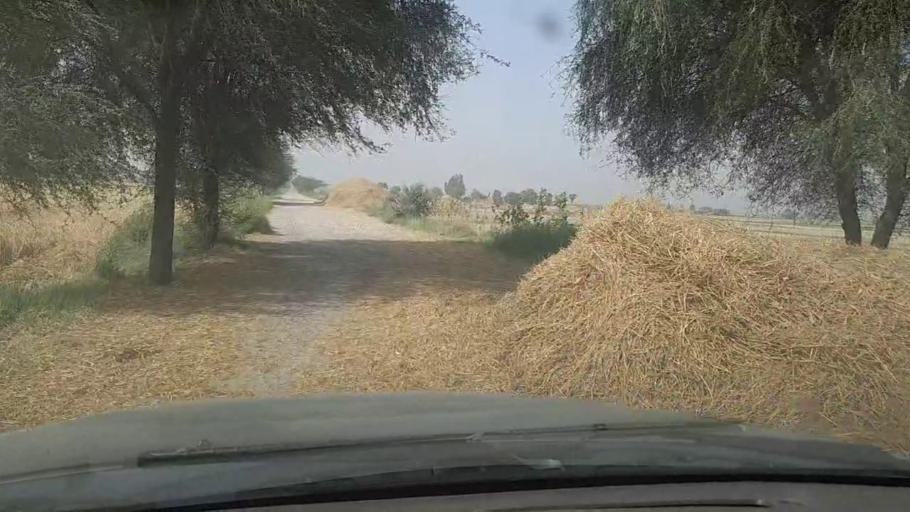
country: PK
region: Sindh
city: Garhi Yasin
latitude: 27.8881
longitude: 68.5770
